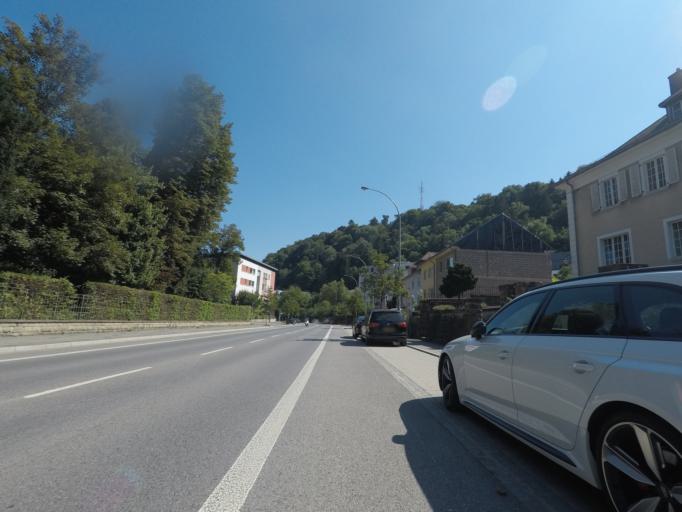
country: LU
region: Luxembourg
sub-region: Canton de Luxembourg
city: Luxembourg
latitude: 49.6273
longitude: 6.1231
